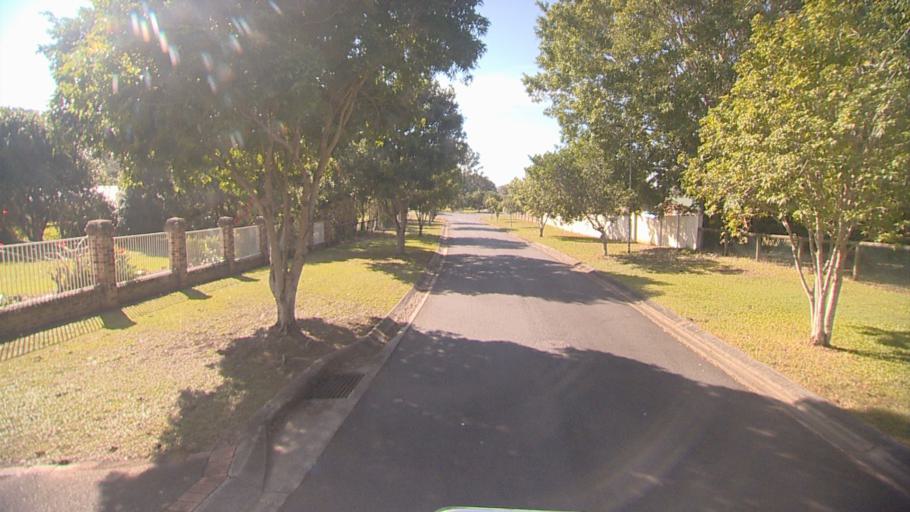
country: AU
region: Queensland
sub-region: Logan
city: Windaroo
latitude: -27.7582
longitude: 153.1785
